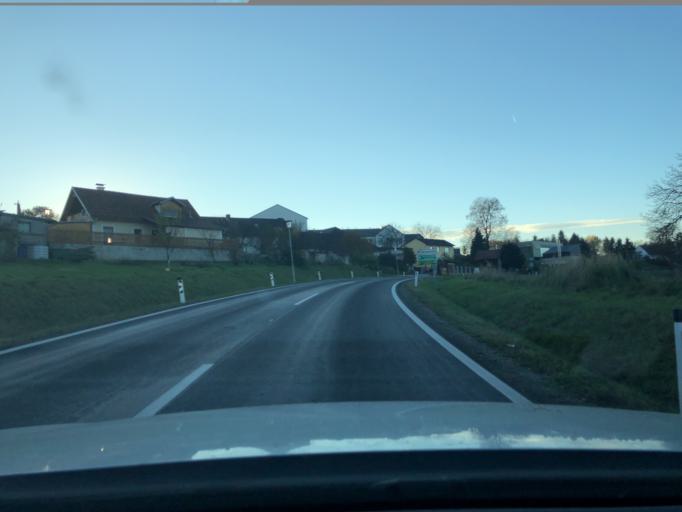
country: AT
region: Styria
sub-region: Politischer Bezirk Weiz
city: Nitscha
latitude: 47.0952
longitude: 15.7573
